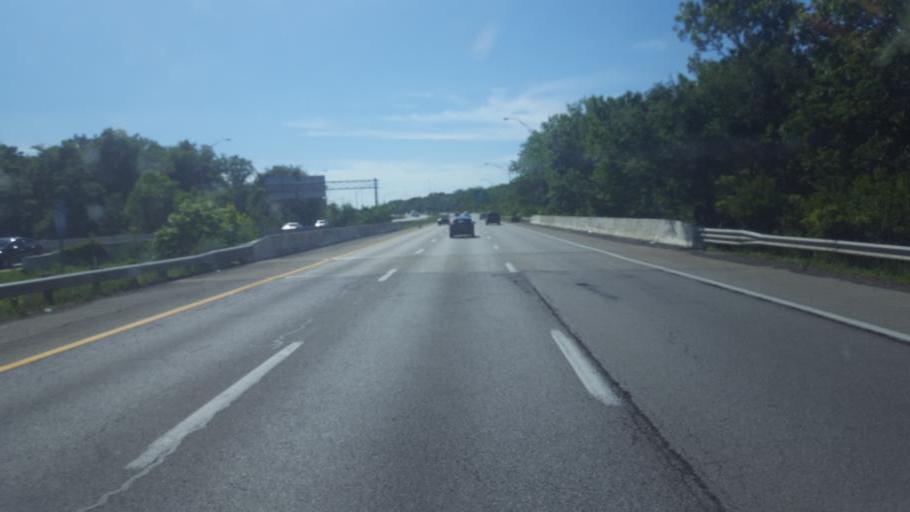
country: US
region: Ohio
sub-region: Franklin County
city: Blacklick Estates
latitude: 39.9355
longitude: -82.8638
